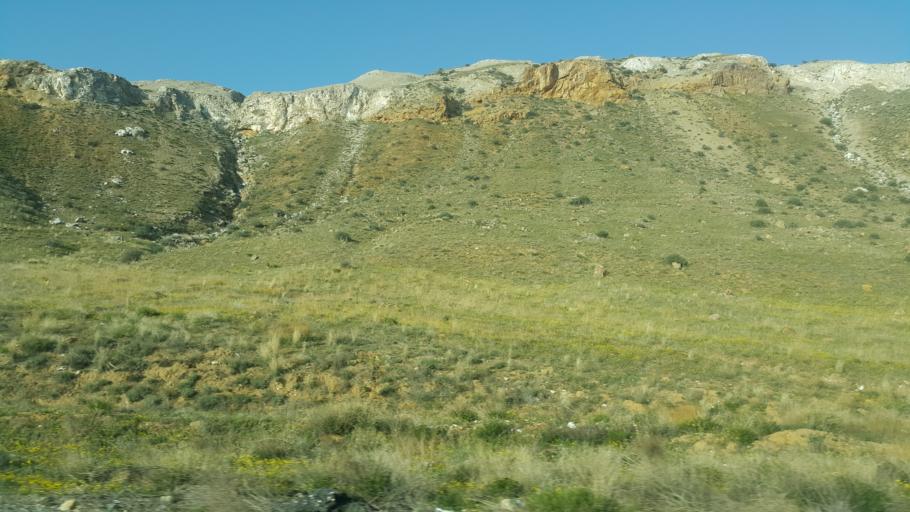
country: TR
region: Ankara
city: Sereflikochisar
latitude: 39.0131
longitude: 33.4547
